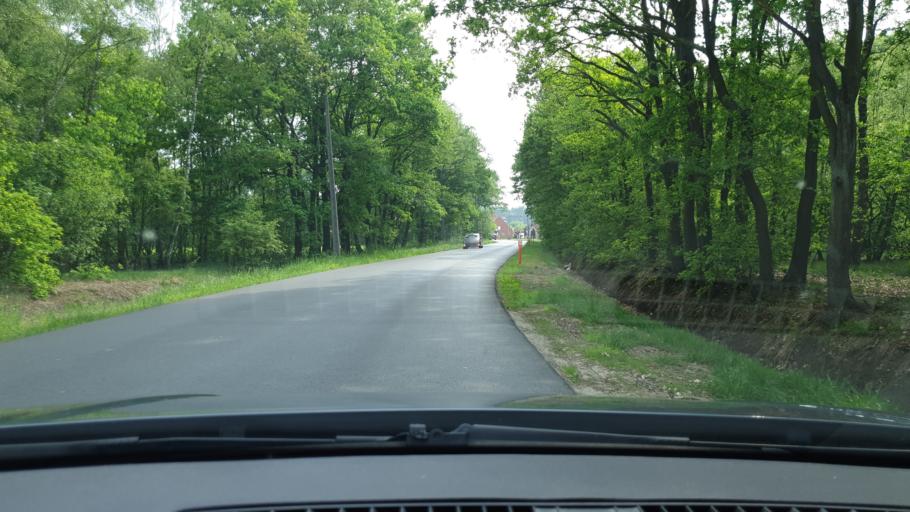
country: BE
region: Flanders
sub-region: Provincie Antwerpen
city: Olen
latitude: 51.1773
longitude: 4.8828
